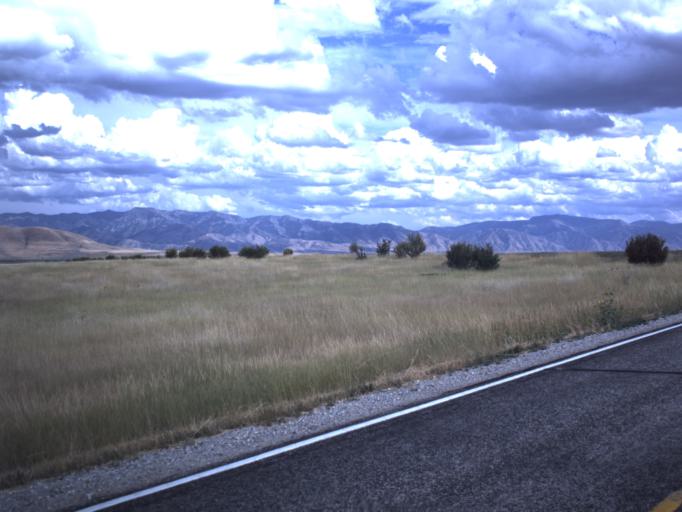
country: US
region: Utah
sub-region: Cache County
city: Benson
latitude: 41.8958
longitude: -112.0435
